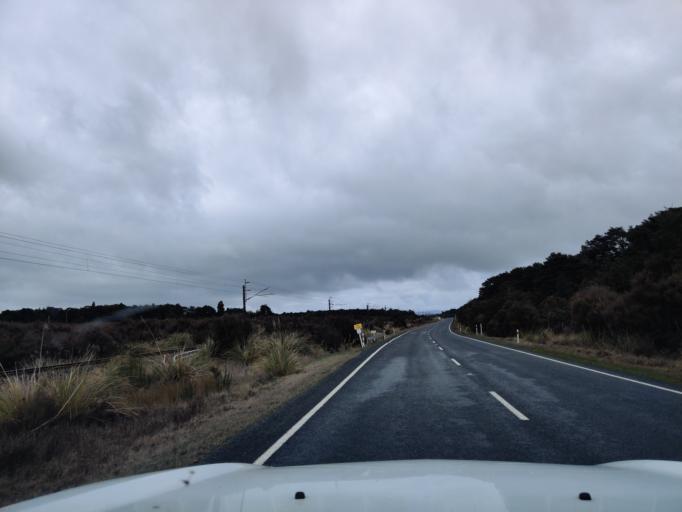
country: NZ
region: Manawatu-Wanganui
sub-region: Ruapehu District
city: Waiouru
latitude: -39.3225
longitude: 175.3854
